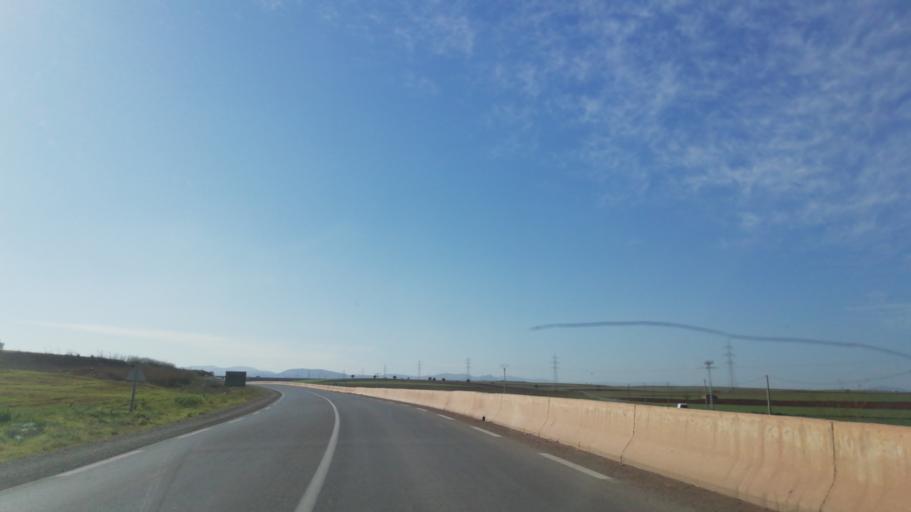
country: DZ
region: Tlemcen
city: Ouled Mimoun
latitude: 35.0180
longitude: -0.9039
